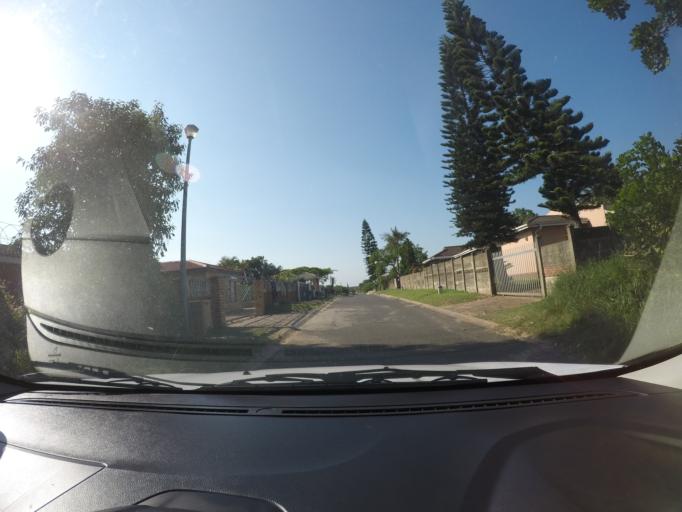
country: ZA
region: KwaZulu-Natal
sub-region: uThungulu District Municipality
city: Richards Bay
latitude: -28.7177
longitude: 32.0335
